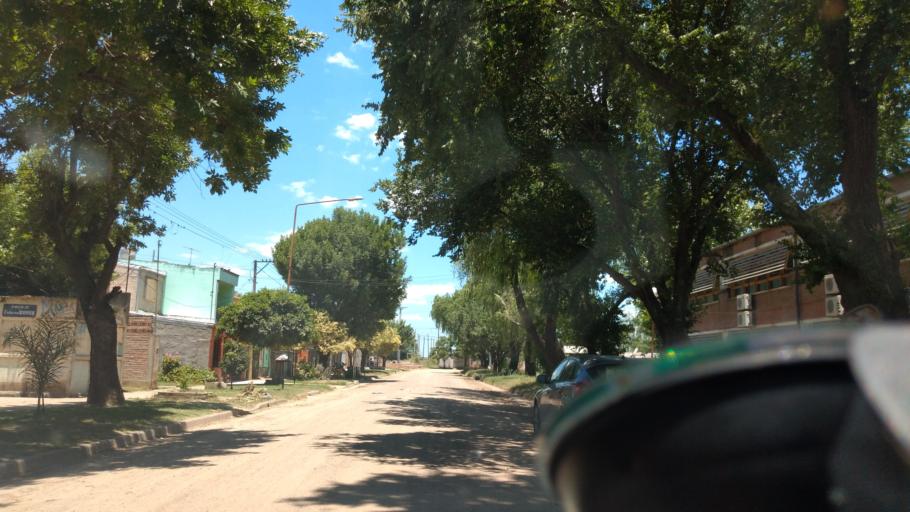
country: AR
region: Santa Fe
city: Laguna Paiva
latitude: -31.3119
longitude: -60.6634
